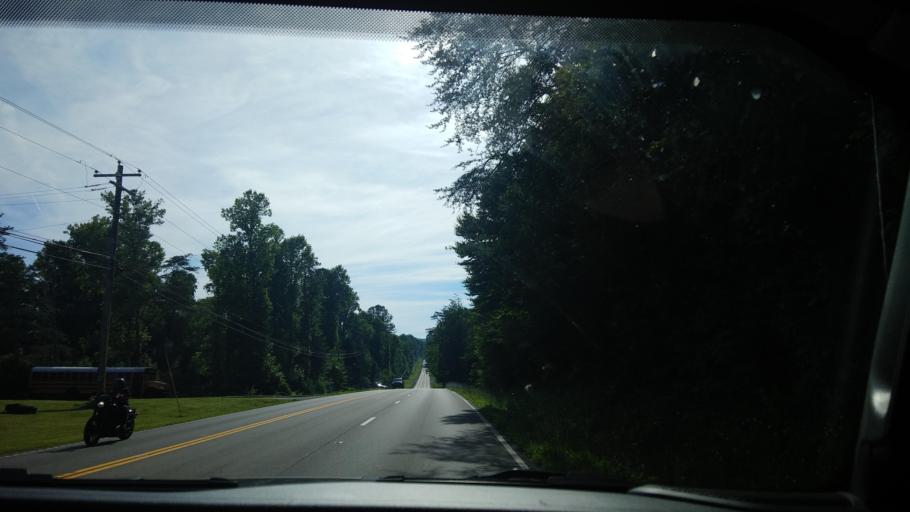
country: US
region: Tennessee
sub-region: Sevier County
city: Gatlinburg
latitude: 35.7596
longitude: -83.3446
